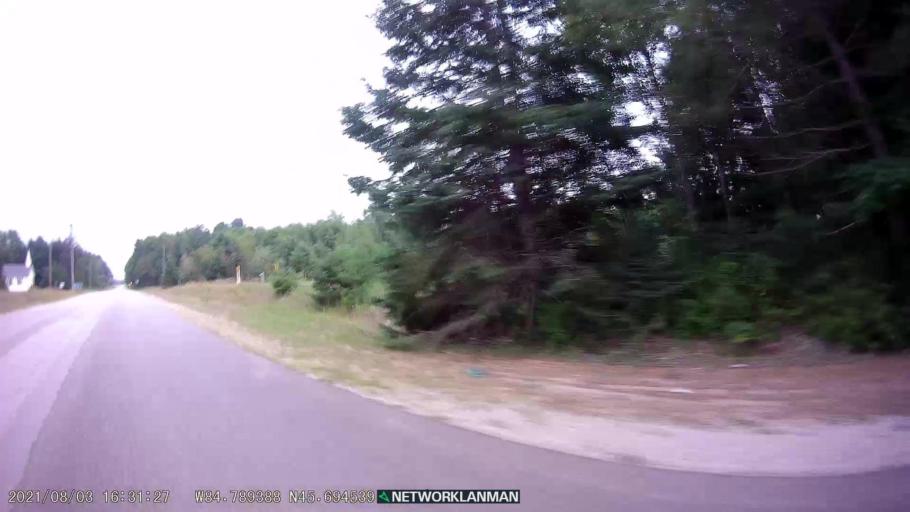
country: US
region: Michigan
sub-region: Mackinac County
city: Saint Ignace
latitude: 45.6945
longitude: -84.7891
